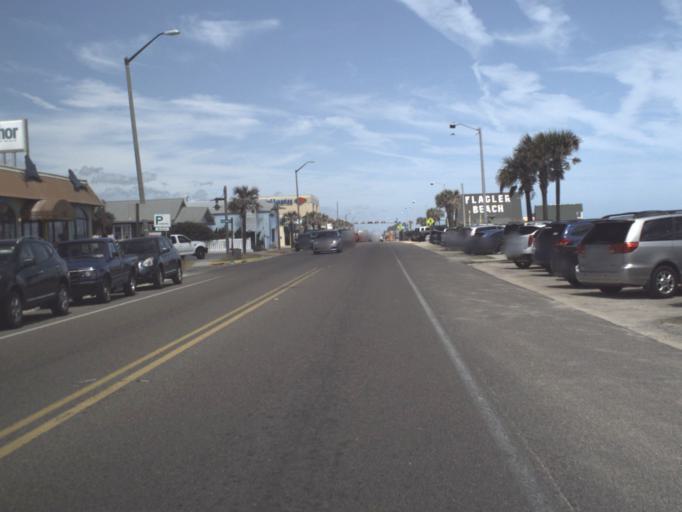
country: US
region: Florida
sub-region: Flagler County
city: Flagler Beach
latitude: 29.4780
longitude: -81.1259
